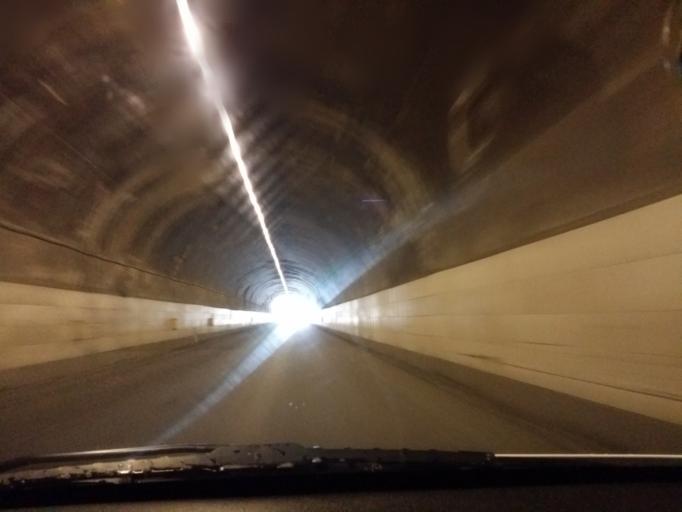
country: IR
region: Alborz
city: Karaj
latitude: 35.9795
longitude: 51.0932
